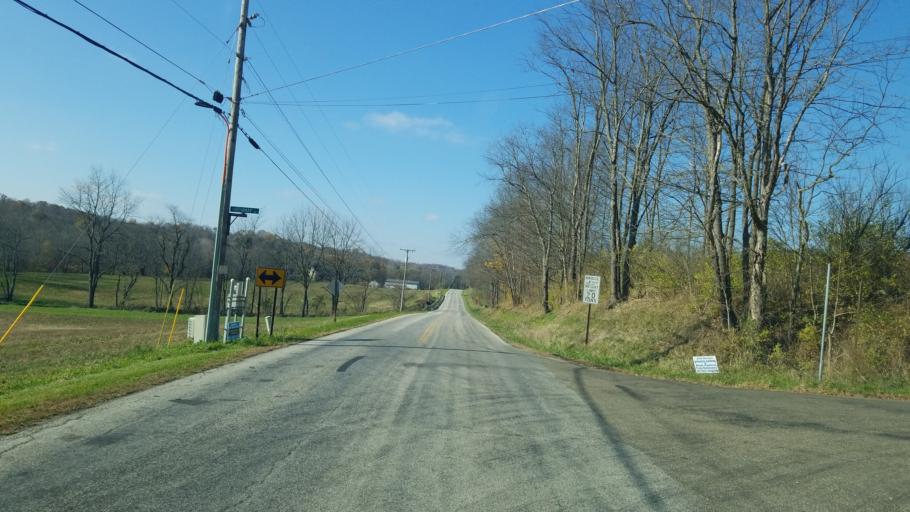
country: US
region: Ohio
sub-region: Sandusky County
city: Bellville
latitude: 40.6476
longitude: -82.4726
